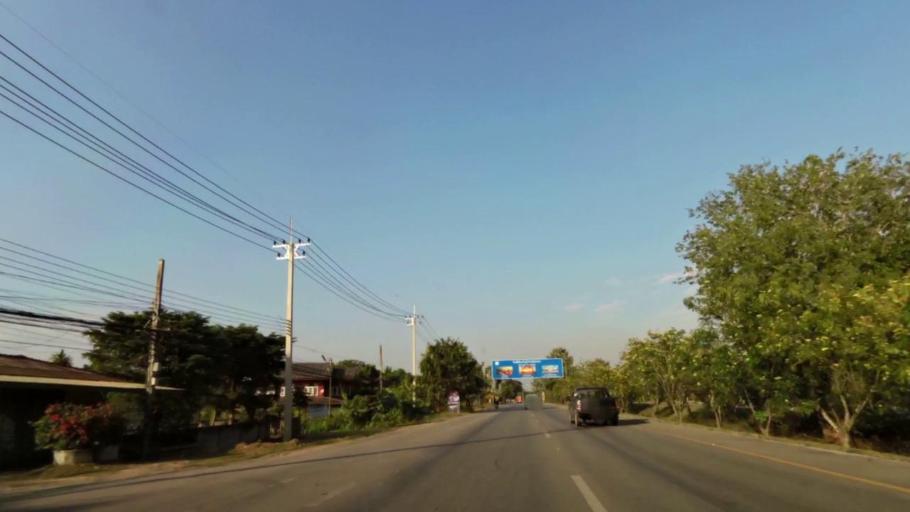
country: TH
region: Phayao
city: Phayao
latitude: 19.1250
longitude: 99.9087
